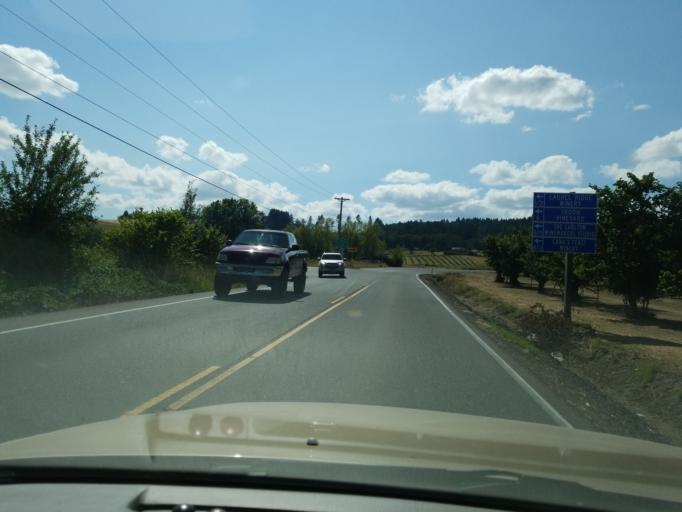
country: US
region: Oregon
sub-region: Yamhill County
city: Lafayette
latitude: 45.3206
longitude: -123.0903
